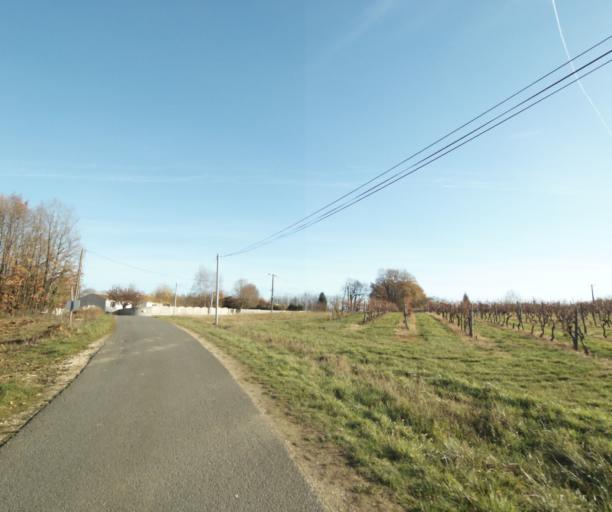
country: FR
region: Poitou-Charentes
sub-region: Departement de la Charente-Maritime
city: Burie
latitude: 45.7749
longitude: -0.4315
